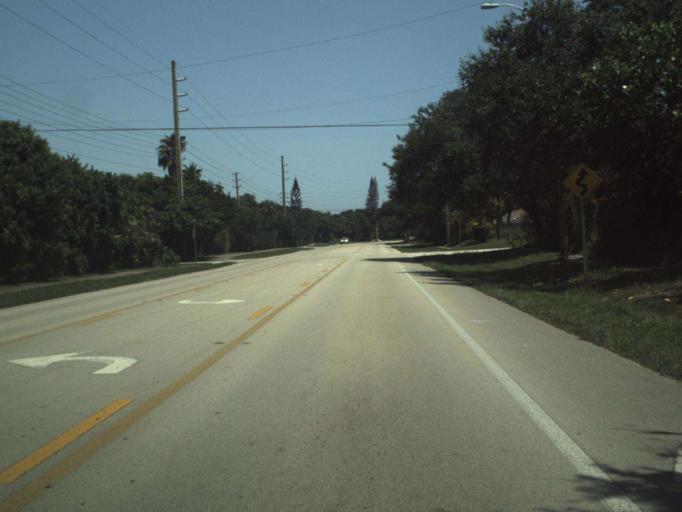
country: US
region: Florida
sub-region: Indian River County
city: Vero Beach
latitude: 27.6607
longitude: -80.3612
